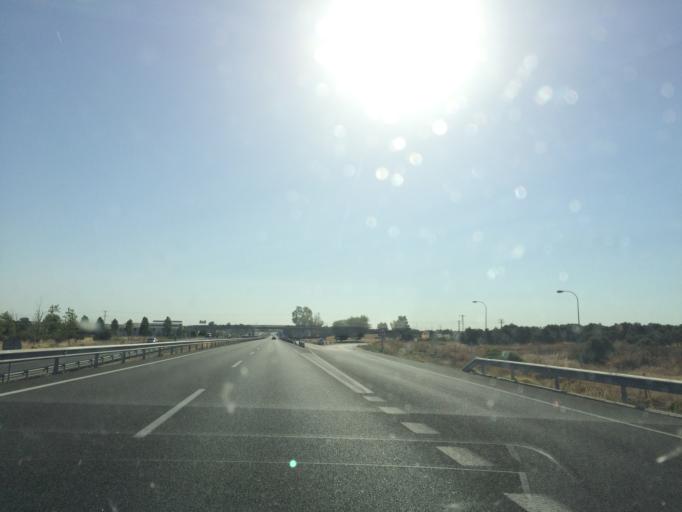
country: ES
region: Castille-La Mancha
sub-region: Province of Toledo
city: Otero
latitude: 40.0193
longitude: -4.5240
